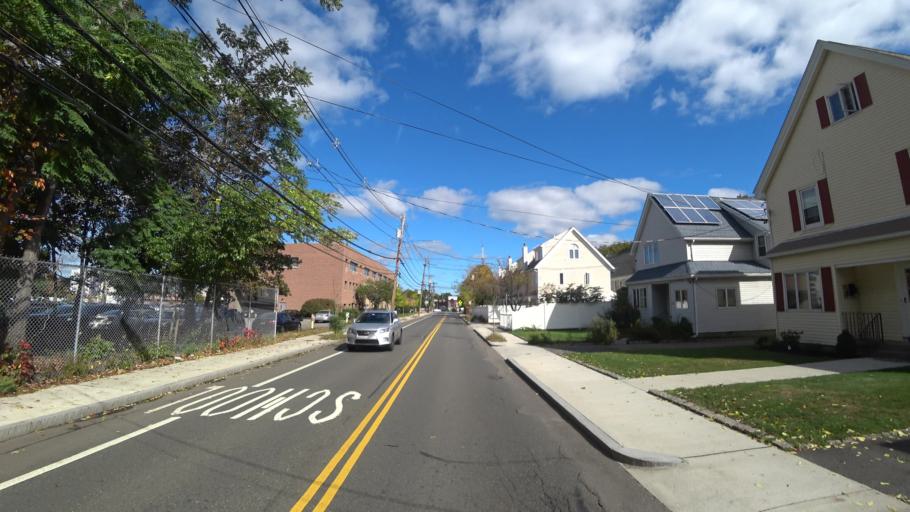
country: US
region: Massachusetts
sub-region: Norfolk County
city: Brookline
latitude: 42.3612
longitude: -71.1362
